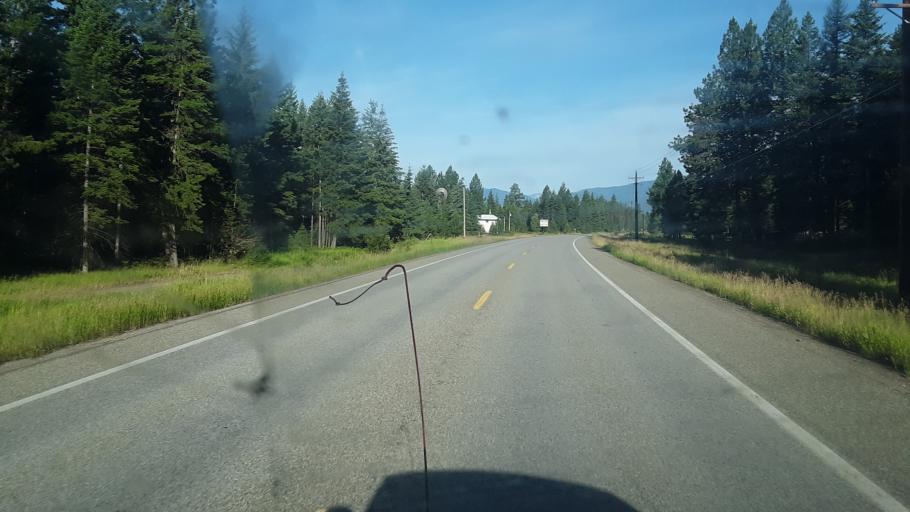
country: US
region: Idaho
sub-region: Boundary County
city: Bonners Ferry
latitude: 48.7266
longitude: -116.2083
